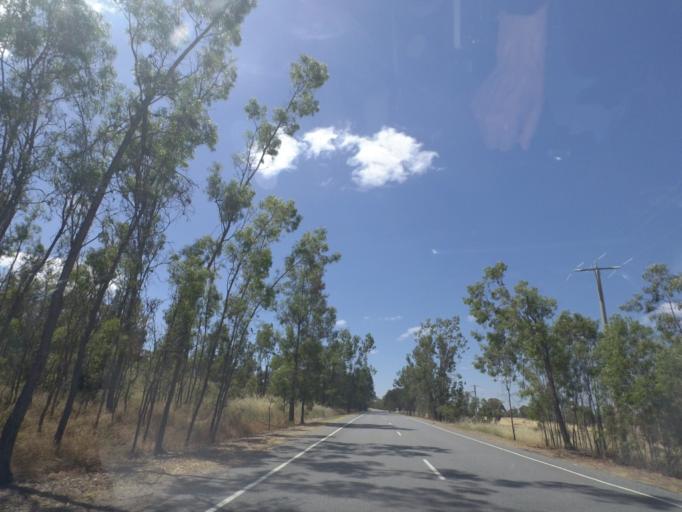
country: AU
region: Victoria
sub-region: Wangaratta
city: Wangaratta
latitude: -36.4547
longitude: 146.2372
